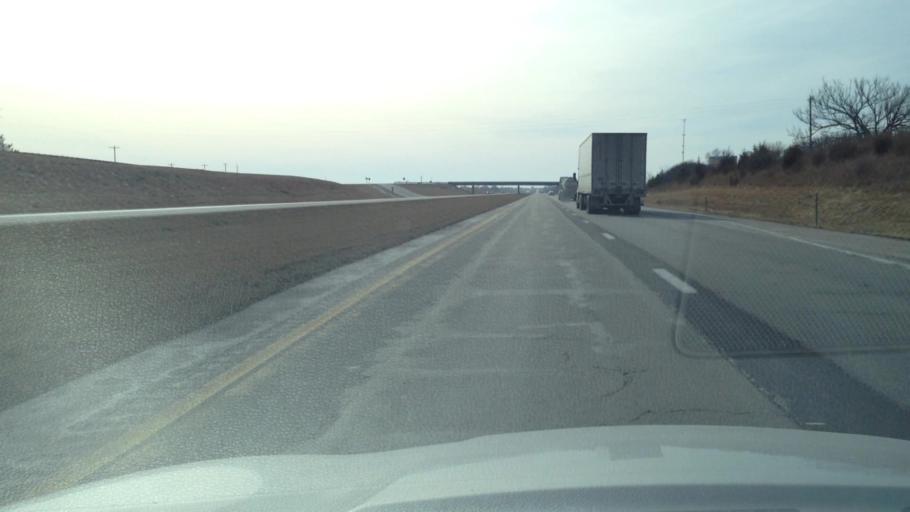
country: US
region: Missouri
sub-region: Harrison County
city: Bethany
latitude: 40.3794
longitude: -94.0017
